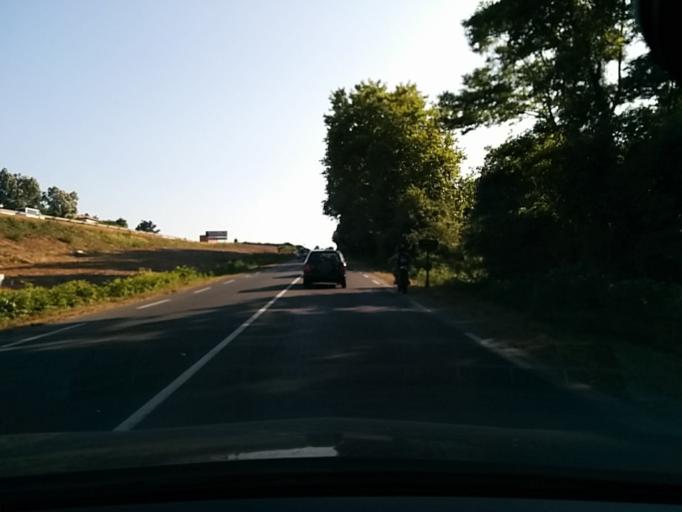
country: FR
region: Aquitaine
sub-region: Departement des Pyrenees-Atlantiques
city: Guethary
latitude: 43.4156
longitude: -1.6117
